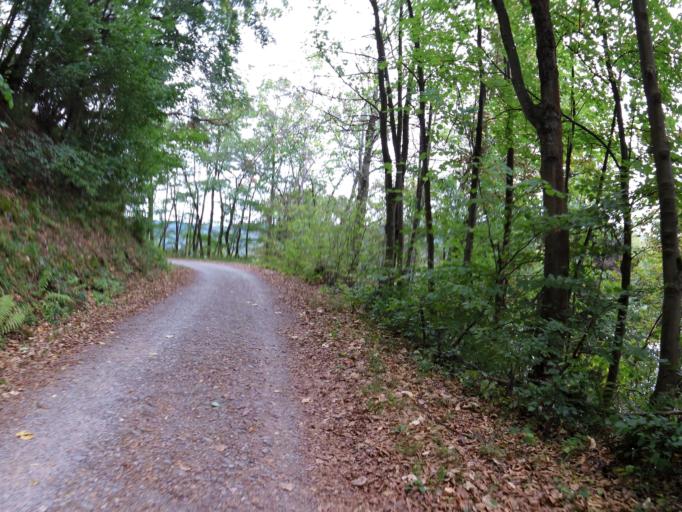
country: DE
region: North Rhine-Westphalia
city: Heimbach
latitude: 50.6343
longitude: 6.4386
